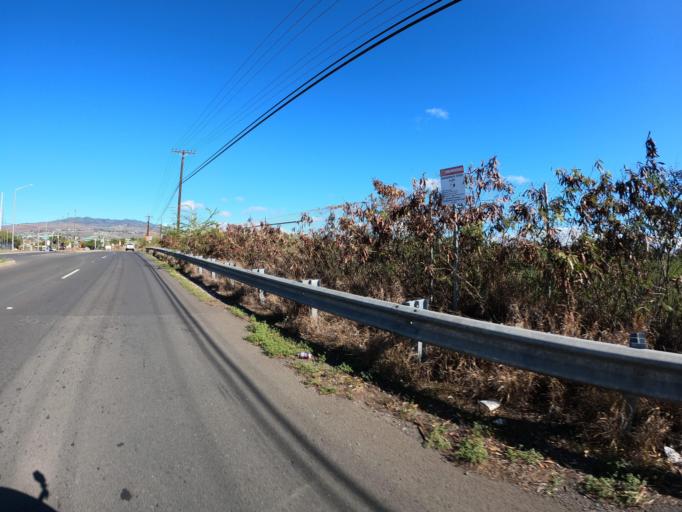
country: US
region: Hawaii
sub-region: Honolulu County
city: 'Ewa Villages
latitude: 21.3236
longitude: -158.0670
